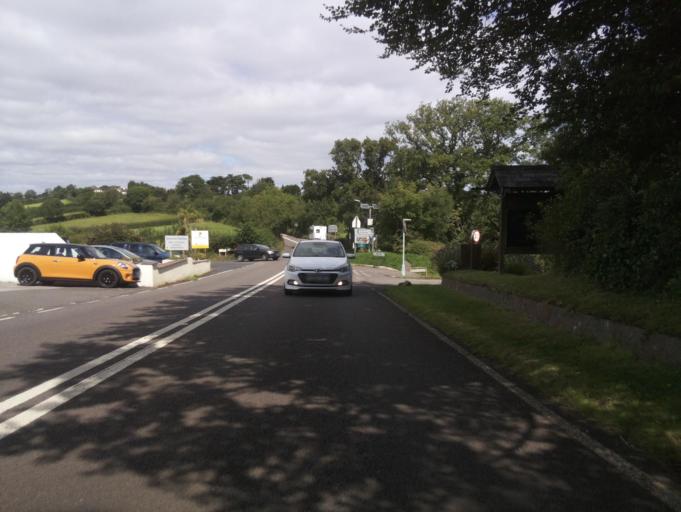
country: GB
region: England
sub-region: Borough of Torbay
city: Torquay
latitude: 50.5075
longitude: -3.5195
